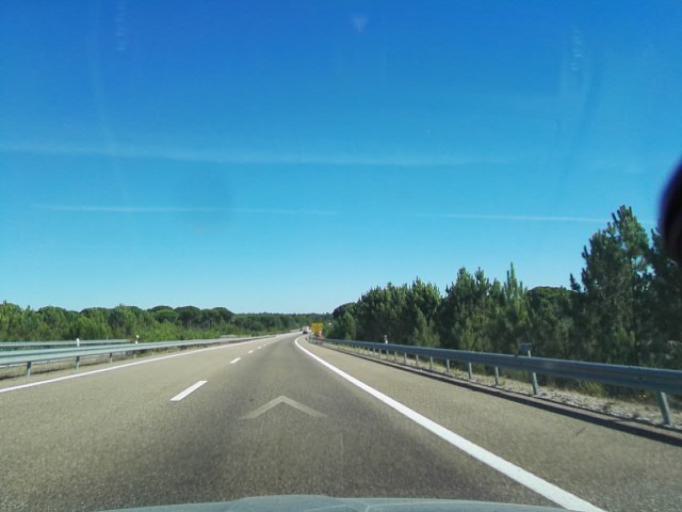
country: PT
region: Evora
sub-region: Vendas Novas
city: Vendas Novas
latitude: 38.6496
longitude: -8.6654
